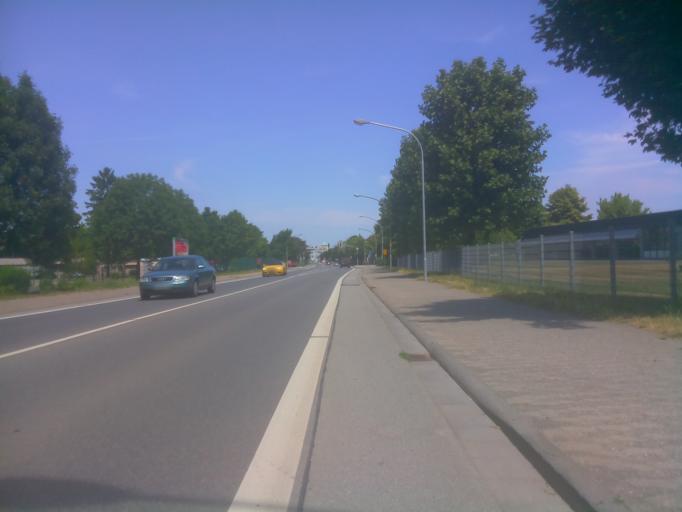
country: DE
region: Hesse
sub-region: Regierungsbezirk Darmstadt
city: Heppenheim an der Bergstrasse
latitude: 49.6345
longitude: 8.6192
